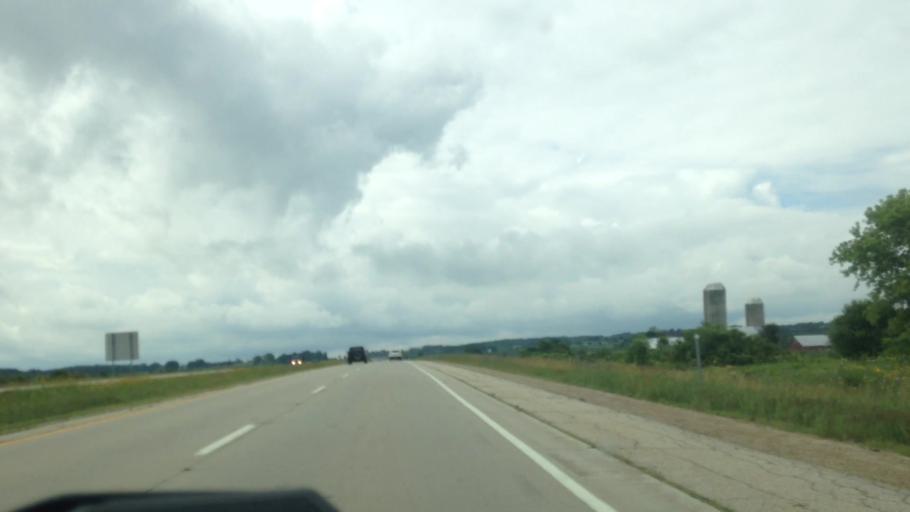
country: US
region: Wisconsin
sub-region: Washington County
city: Jackson
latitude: 43.3133
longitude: -88.1824
